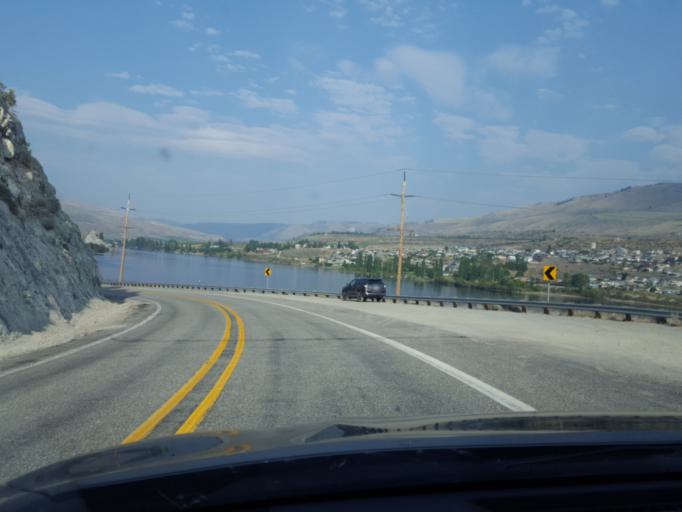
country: US
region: Washington
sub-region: Chelan County
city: Entiat
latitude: 47.7667
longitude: -120.1796
